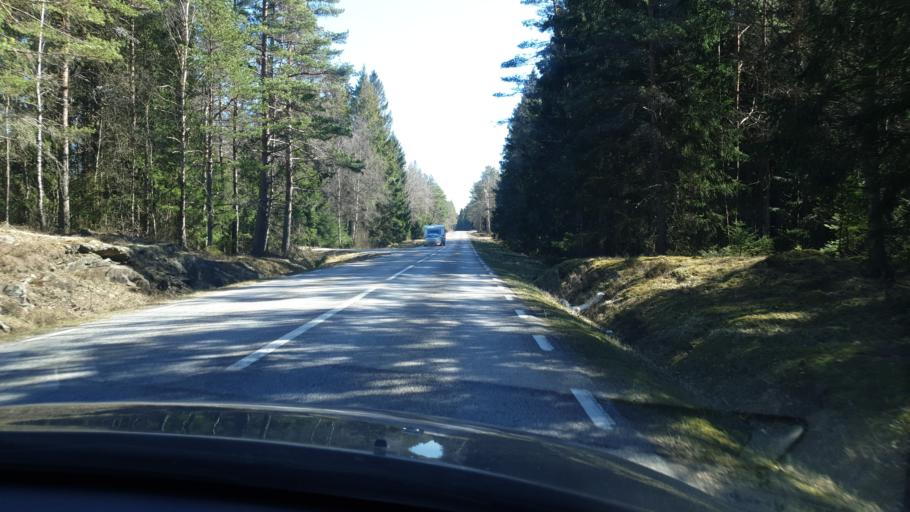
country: SE
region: Vaestra Goetaland
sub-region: Tanums Kommun
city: Tanumshede
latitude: 58.7426
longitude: 11.4606
